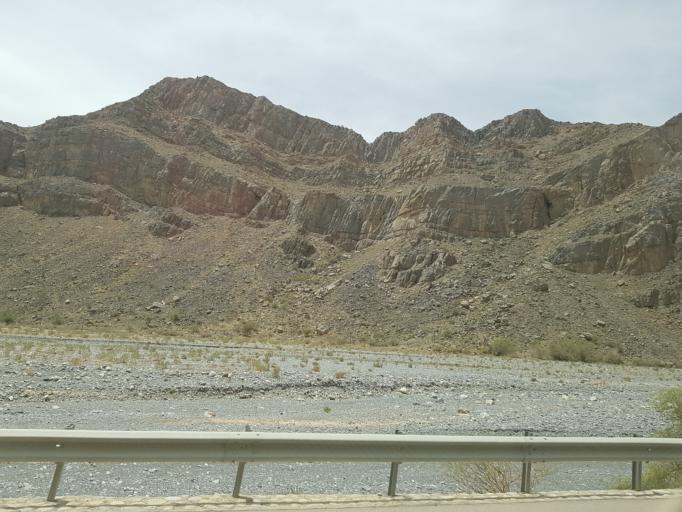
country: OM
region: Muhafazat ad Dakhiliyah
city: Izki
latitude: 22.9430
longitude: 57.6734
